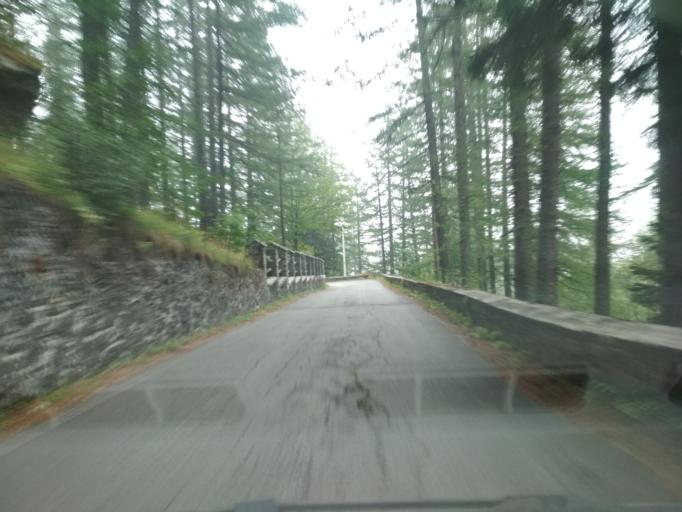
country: IT
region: Piedmont
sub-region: Provincia di Torino
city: Balme
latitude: 45.3021
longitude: 7.2002
